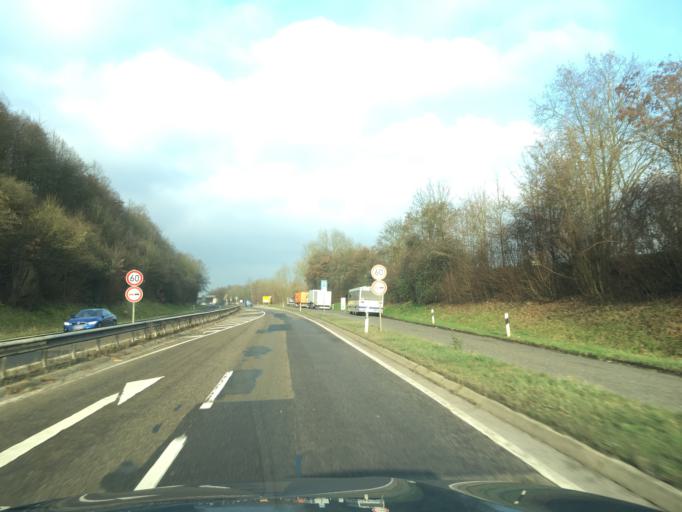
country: DE
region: Rheinland-Pfalz
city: Sinzig
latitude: 50.5633
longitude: 7.2451
